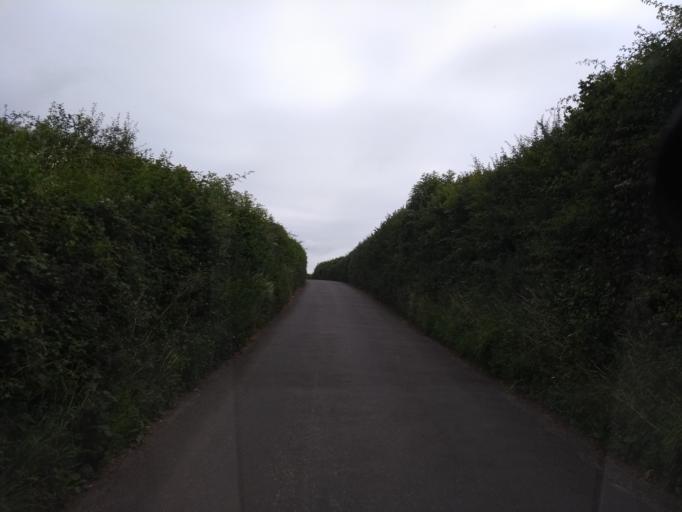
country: GB
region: England
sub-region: Somerset
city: Wiveliscombe
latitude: 51.0305
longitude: -3.2479
